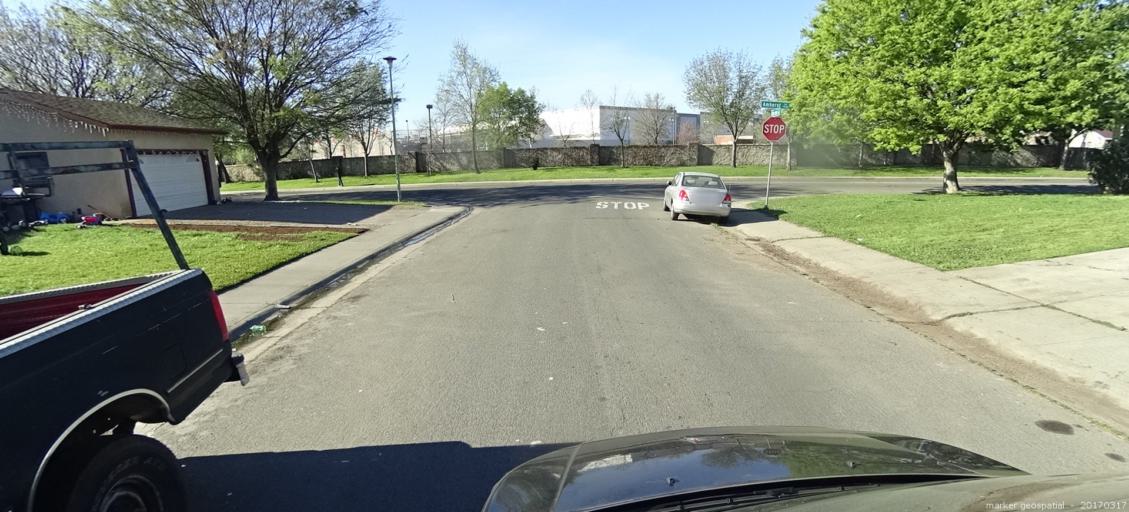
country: US
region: California
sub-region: Sacramento County
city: Parkway
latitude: 38.4843
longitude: -121.5020
